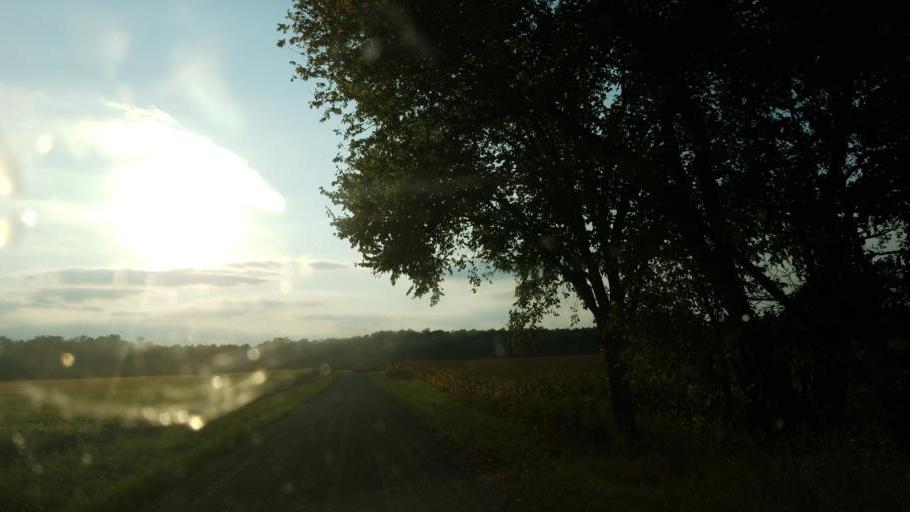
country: US
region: Ohio
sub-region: Knox County
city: Fredericktown
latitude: 40.4092
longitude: -82.6330
